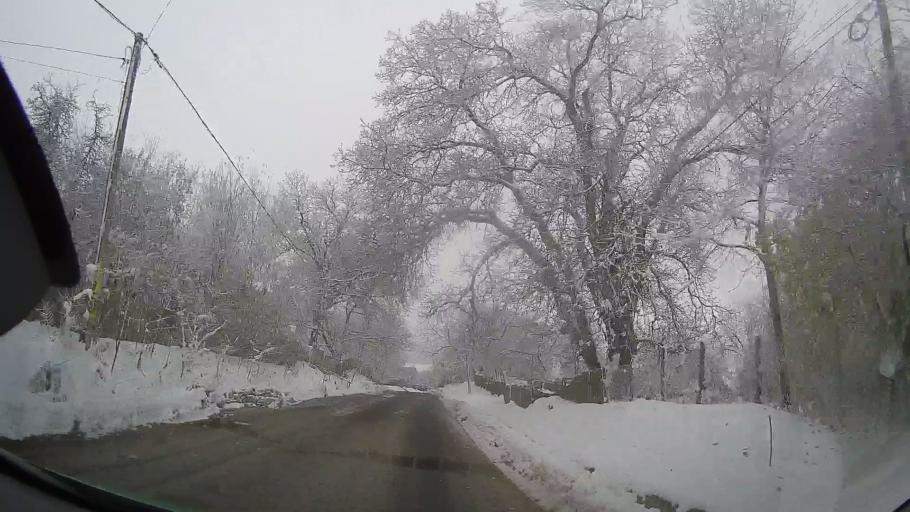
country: RO
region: Neamt
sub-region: Comuna Poenari
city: Poienari
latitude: 46.8894
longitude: 27.1338
